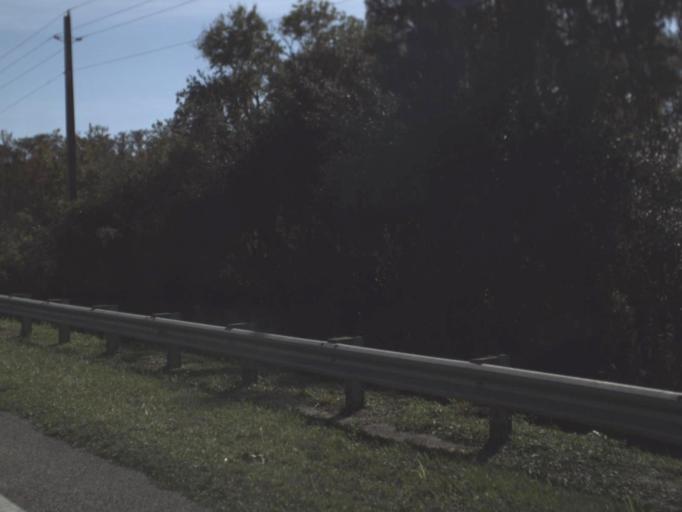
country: US
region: Florida
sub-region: Hendry County
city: Port LaBelle
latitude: 26.9317
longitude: -81.3150
